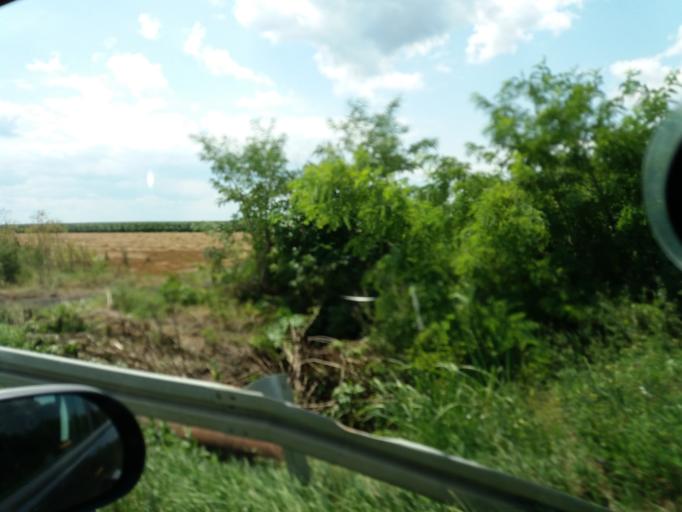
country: RS
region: Autonomna Pokrajina Vojvodina
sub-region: Sremski Okrug
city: Pecinci
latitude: 44.8745
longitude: 19.9618
